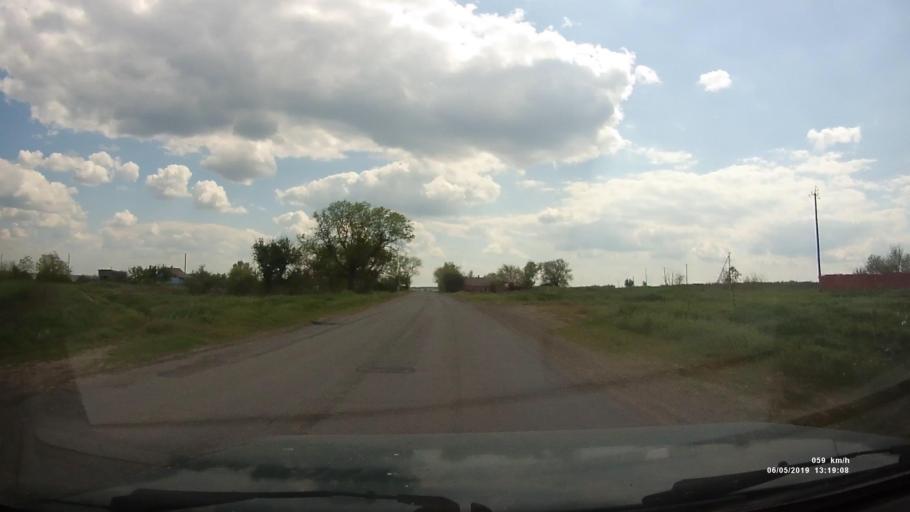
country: RU
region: Rostov
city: Ust'-Donetskiy
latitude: 47.7280
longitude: 40.9140
